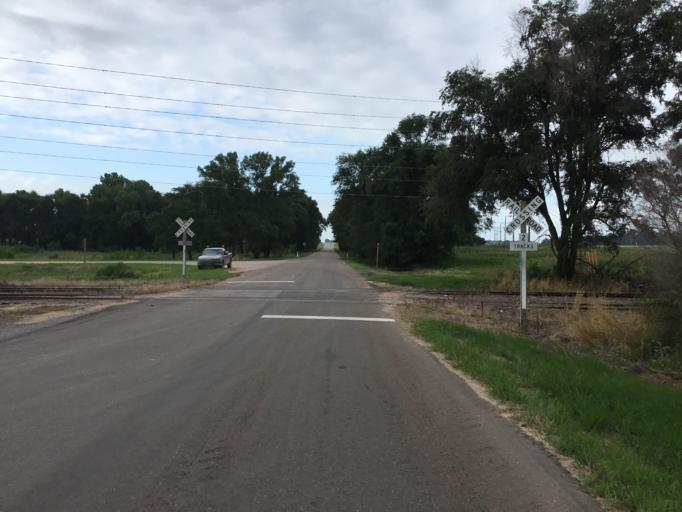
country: US
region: Kansas
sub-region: Pratt County
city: Pratt
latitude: 37.6523
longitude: -98.5568
